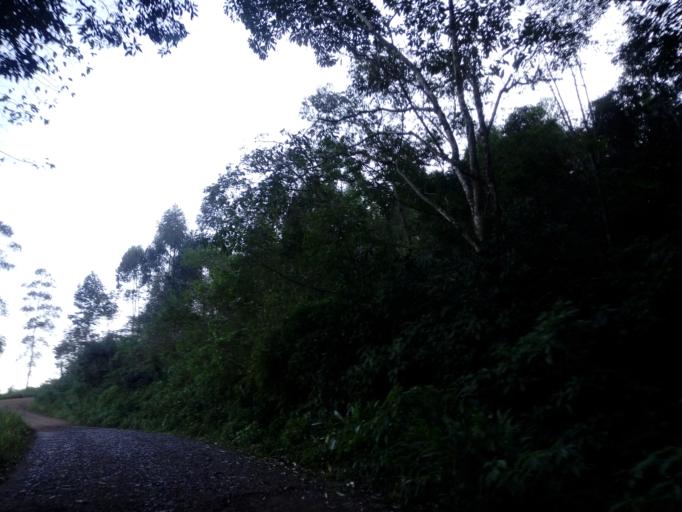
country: BR
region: Santa Catarina
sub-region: Chapeco
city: Chapeco
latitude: -27.2329
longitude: -52.6720
